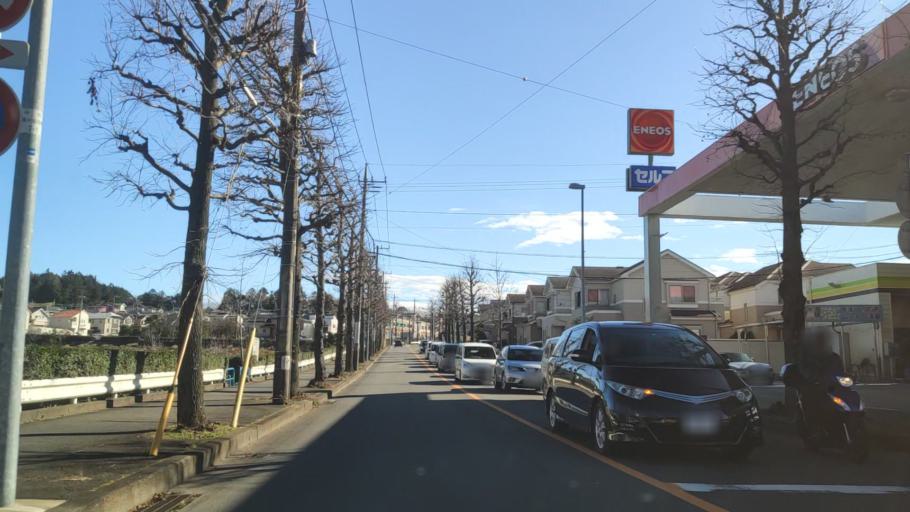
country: JP
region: Tokyo
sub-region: Machida-shi
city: Machida
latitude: 35.5201
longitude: 139.5068
